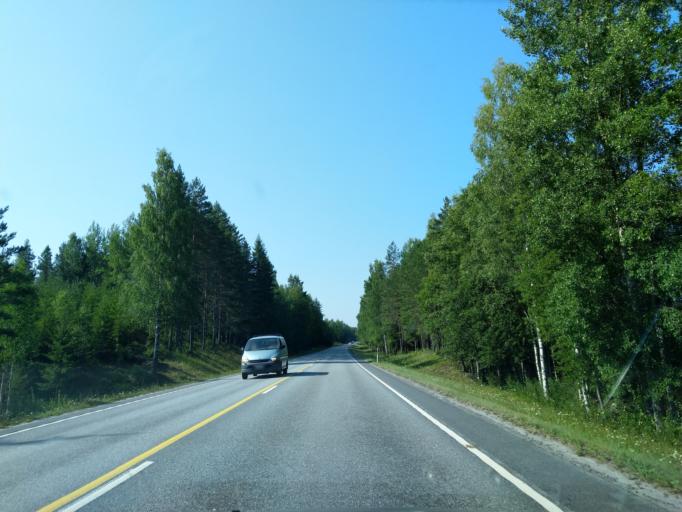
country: FI
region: Satakunta
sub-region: Pori
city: Pomarkku
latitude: 61.6420
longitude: 21.9475
